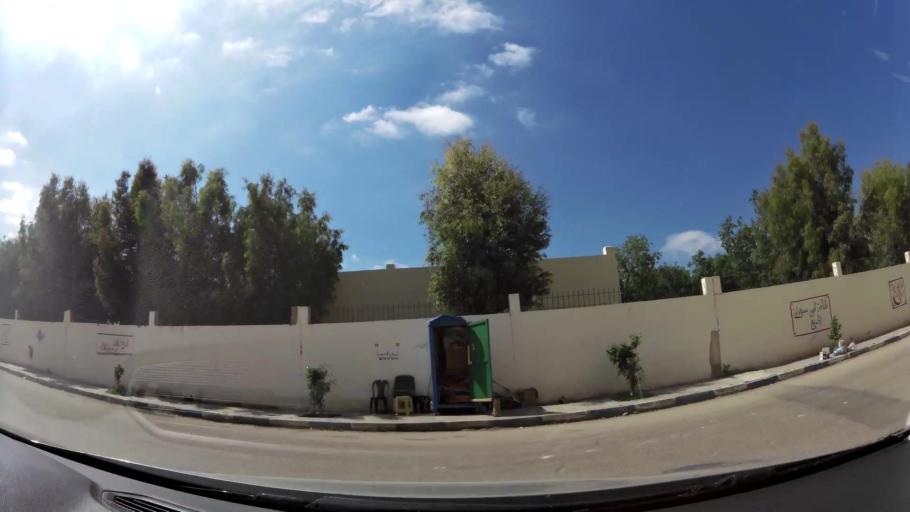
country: MA
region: Fes-Boulemane
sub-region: Fes
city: Fes
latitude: 34.0384
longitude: -5.0297
